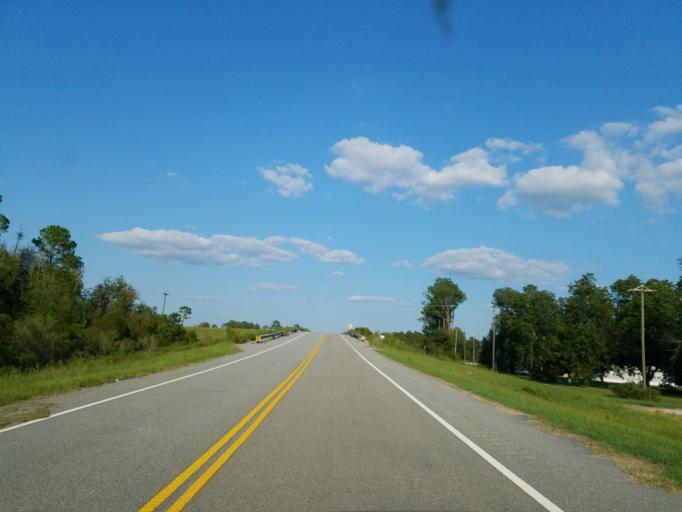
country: US
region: Georgia
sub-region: Cook County
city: Sparks
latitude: 31.2359
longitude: -83.4676
